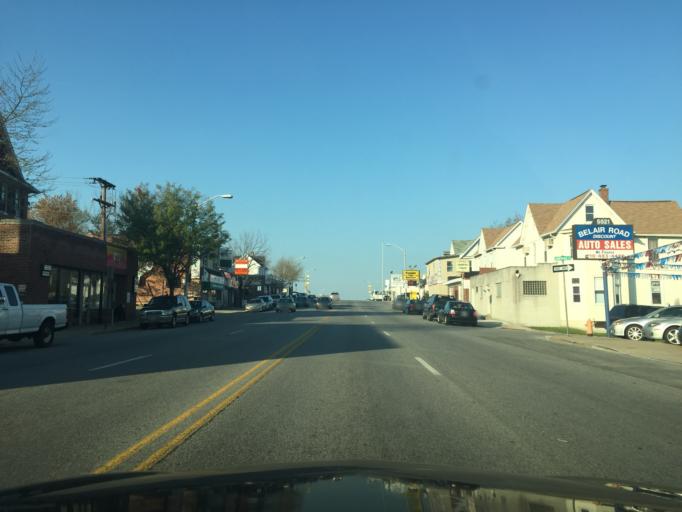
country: US
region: Maryland
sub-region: Baltimore County
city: Overlea
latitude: 39.3397
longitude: -76.5494
